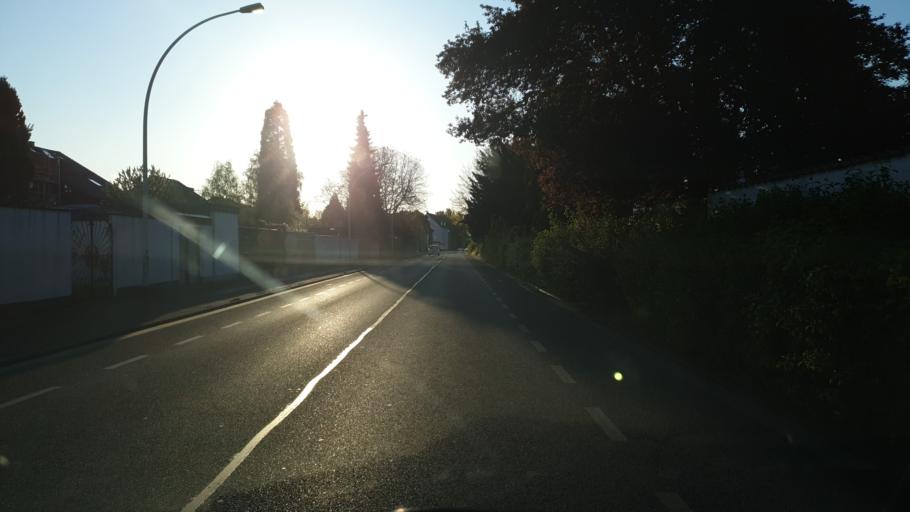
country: DE
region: North Rhine-Westphalia
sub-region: Regierungsbezirk Koln
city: Frechen
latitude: 50.8967
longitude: 6.8233
